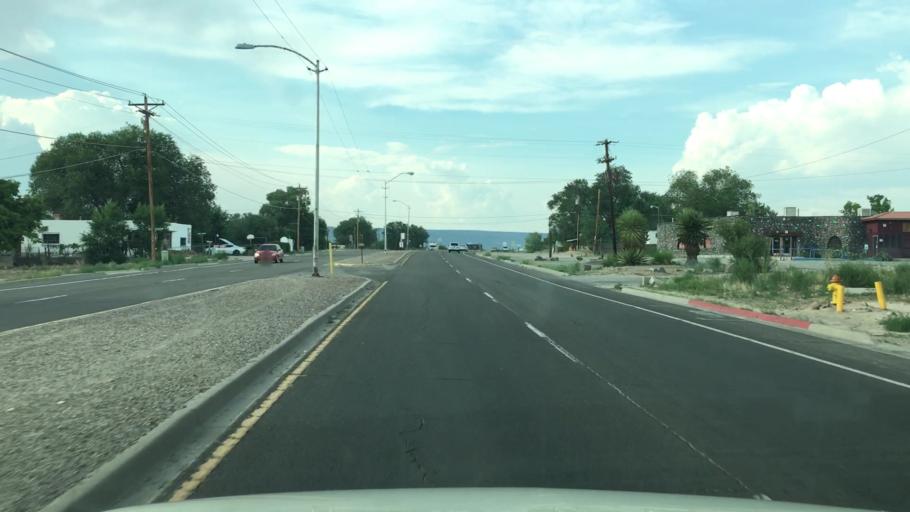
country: US
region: New Mexico
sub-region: Rio Arriba County
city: Ohkay Owingeh
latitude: 36.0281
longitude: -106.0640
